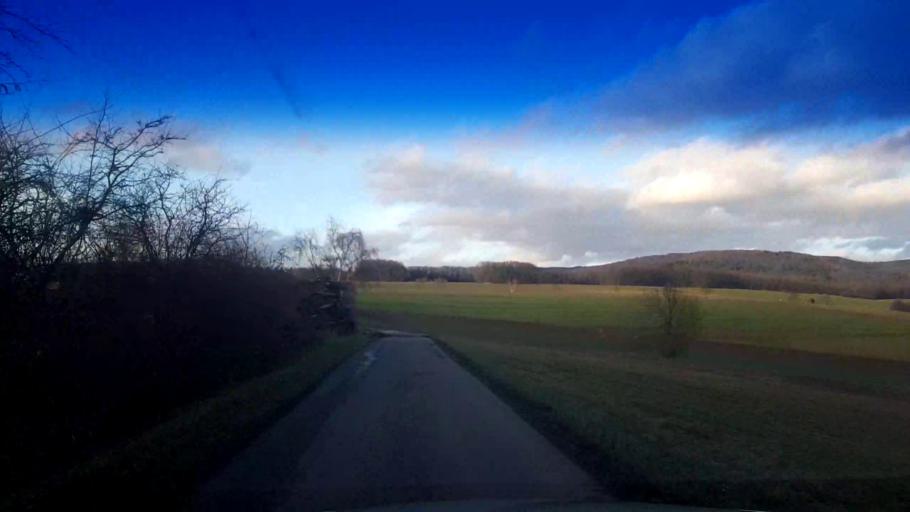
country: DE
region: Bavaria
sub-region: Upper Franconia
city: Buttenheim
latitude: 49.8116
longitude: 11.0388
